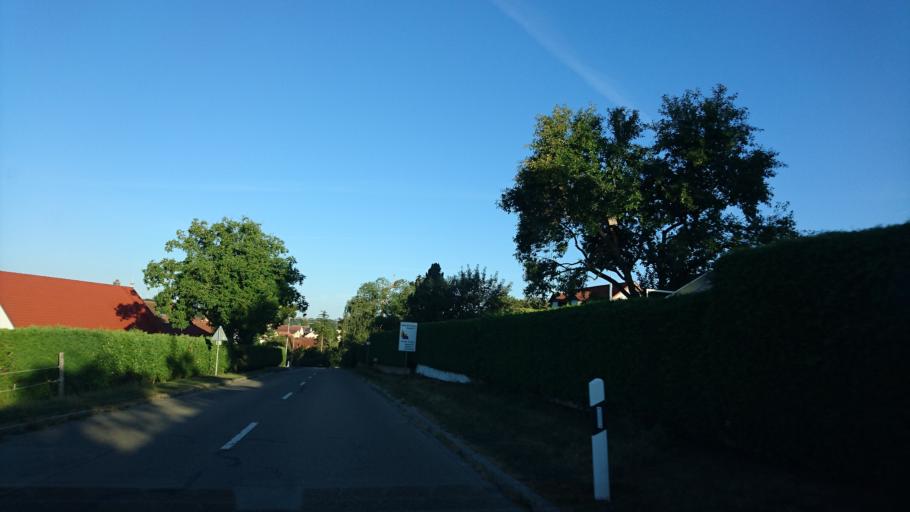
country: DE
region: Bavaria
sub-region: Regierungsbezirk Mittelfranken
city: Nennslingen
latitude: 49.0475
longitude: 11.1391
